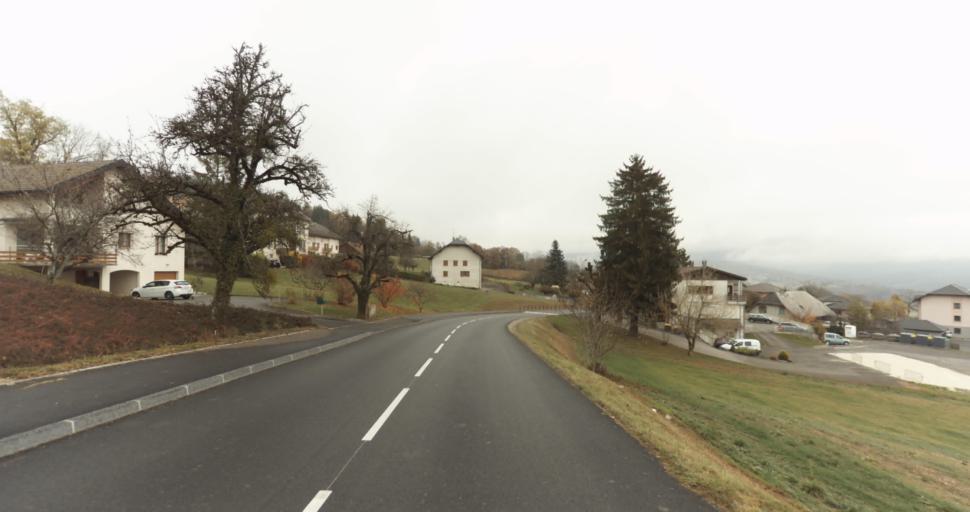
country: FR
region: Rhone-Alpes
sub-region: Departement de la Haute-Savoie
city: Groisy
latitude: 46.0166
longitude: 6.1699
